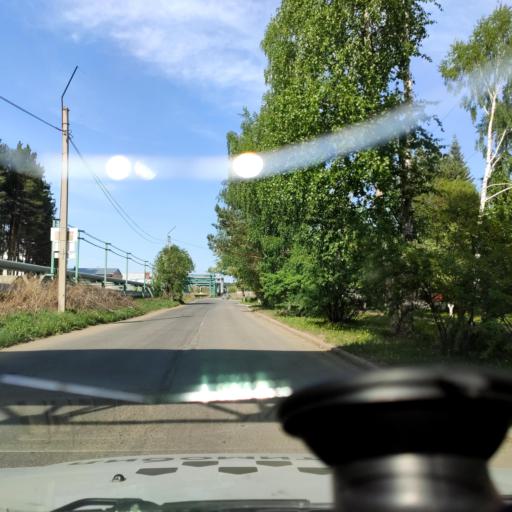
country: RU
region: Sverdlovsk
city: Sovkhoznyy
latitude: 56.7739
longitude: 60.5518
